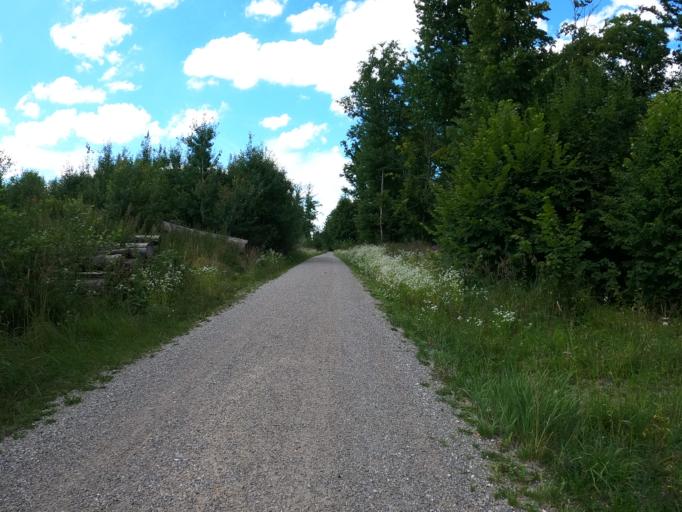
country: DE
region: Bavaria
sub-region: Swabia
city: Leipheim
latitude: 48.4183
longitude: 10.2119
